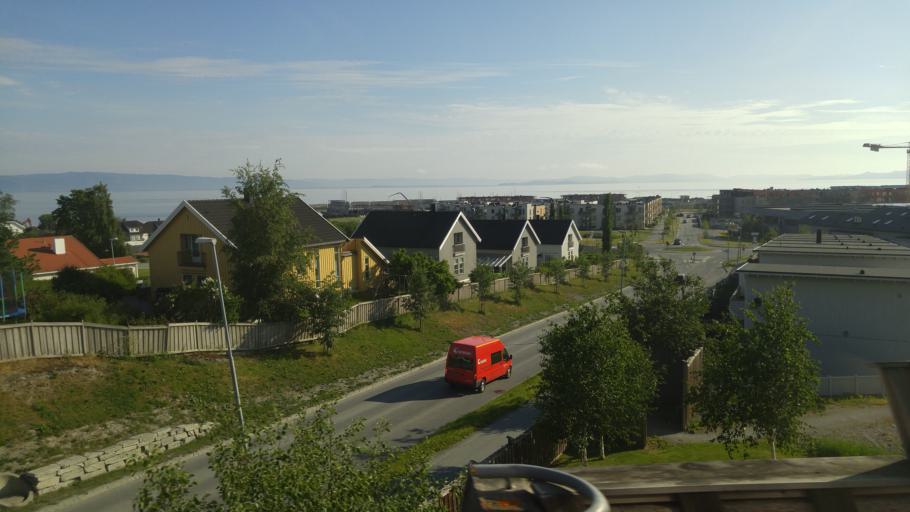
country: NO
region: Sor-Trondelag
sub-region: Trondheim
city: Trondheim
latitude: 63.4328
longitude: 10.4985
